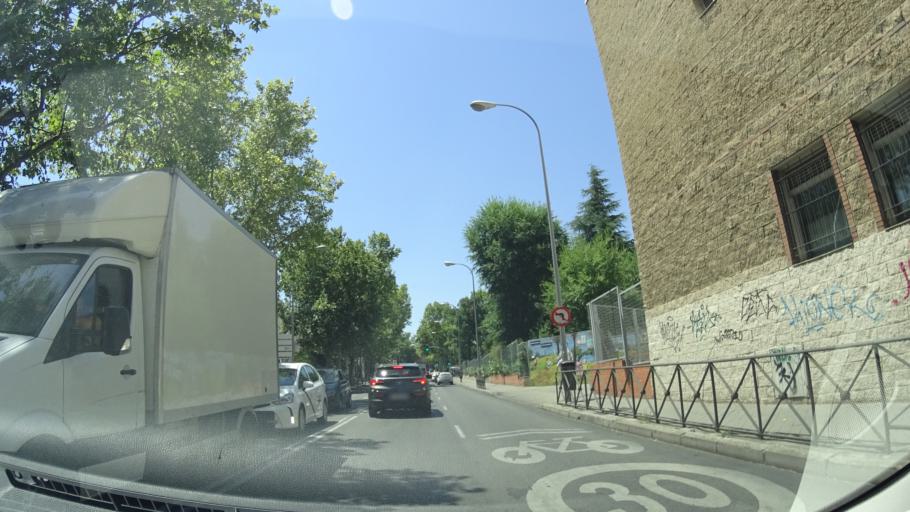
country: ES
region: Madrid
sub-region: Provincia de Madrid
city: Latina
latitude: 40.3777
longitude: -3.7487
